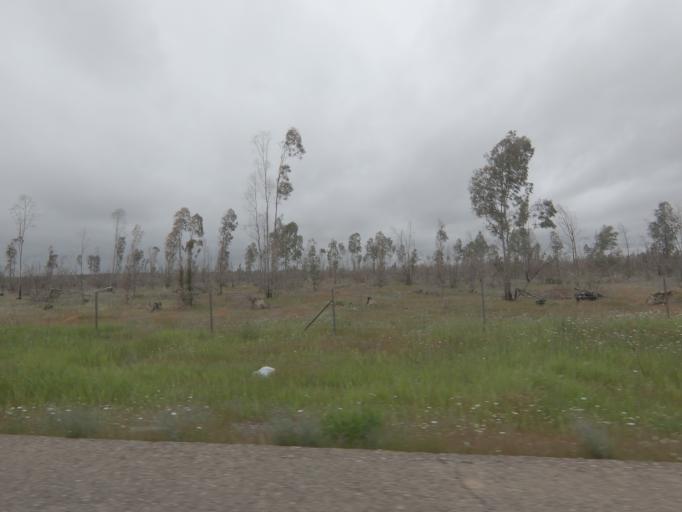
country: ES
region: Extremadura
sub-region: Provincia de Badajoz
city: Badajoz
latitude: 38.9834
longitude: -6.8816
